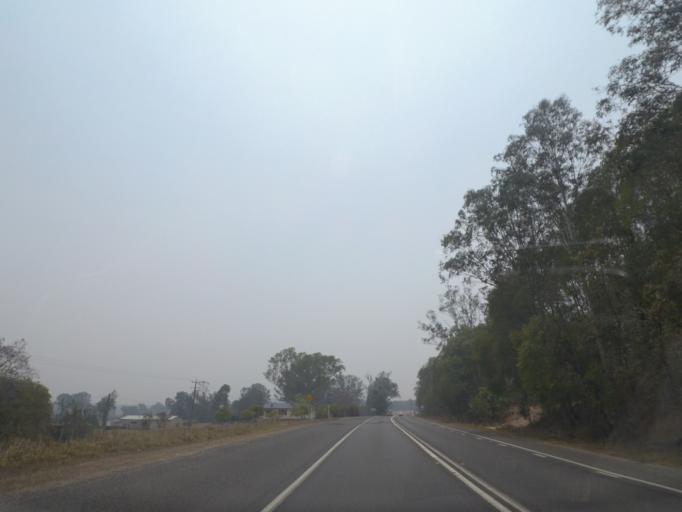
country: AU
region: New South Wales
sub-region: Clarence Valley
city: Maclean
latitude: -29.5538
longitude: 153.1529
